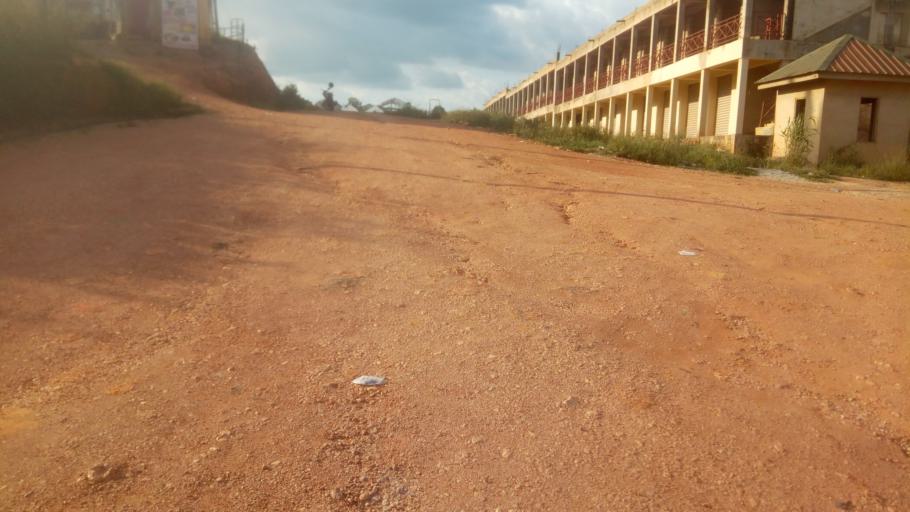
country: GH
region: Ashanti
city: Obuasi
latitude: 6.2131
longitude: -1.6907
